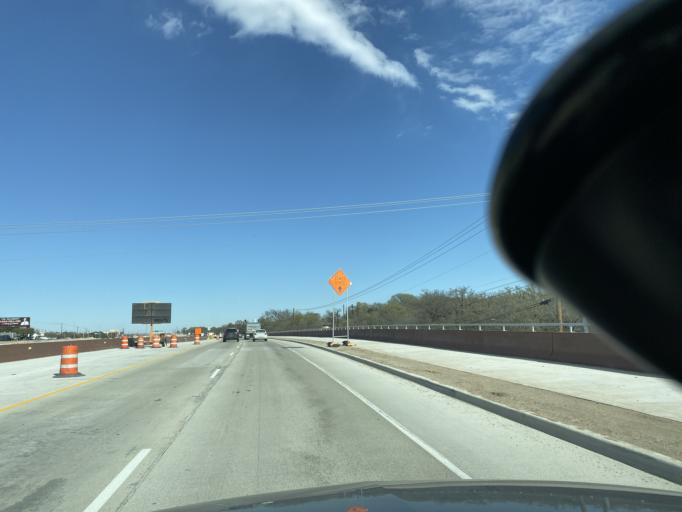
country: US
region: Texas
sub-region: Travis County
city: Austin
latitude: 30.2663
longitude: -97.6705
